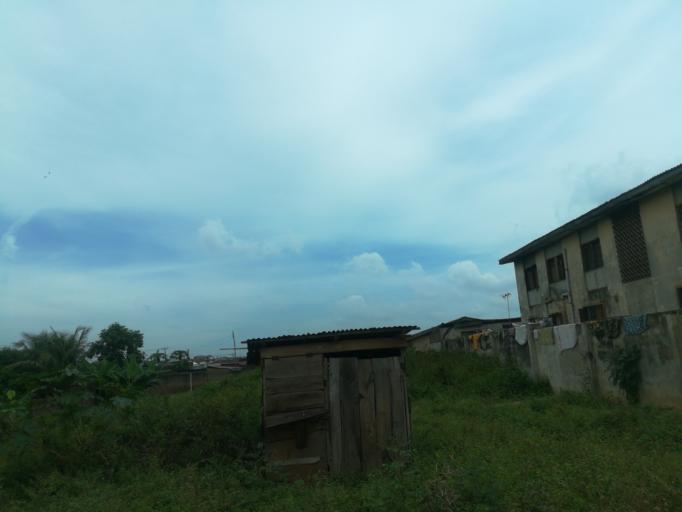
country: NG
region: Oyo
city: Ibadan
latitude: 7.3761
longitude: 3.9527
